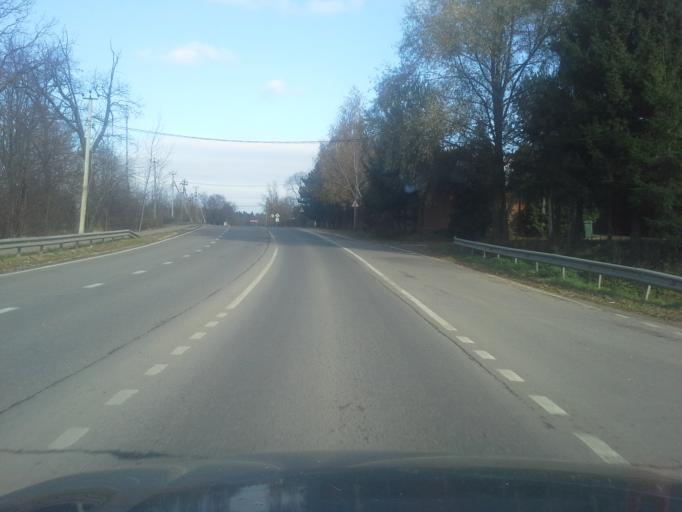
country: RU
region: Moskovskaya
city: Zhavoronki
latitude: 55.6839
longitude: 37.1040
